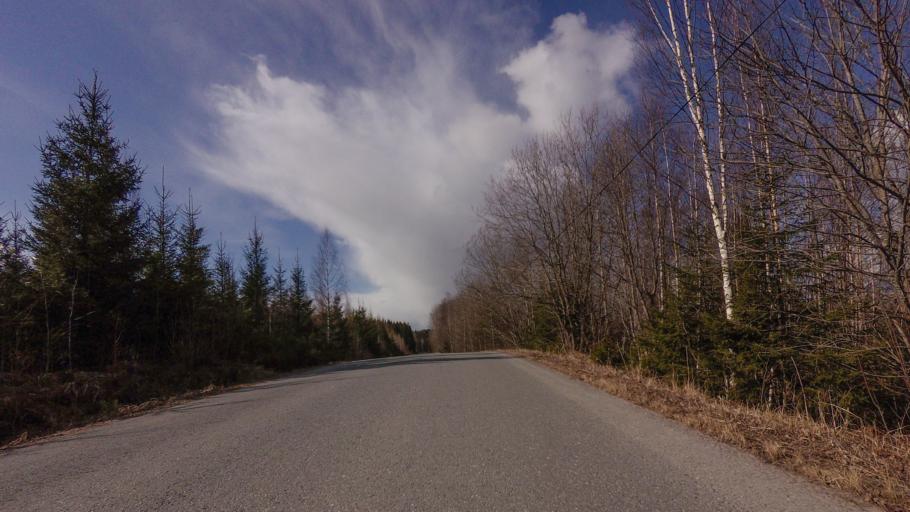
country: FI
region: Varsinais-Suomi
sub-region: Salo
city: Suomusjaervi
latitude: 60.3466
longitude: 23.6764
